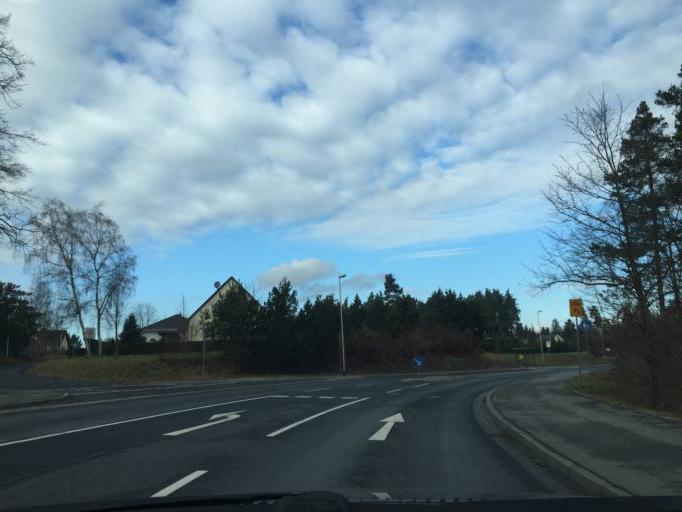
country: DE
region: Saxony
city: Ottendorf-Okrilla
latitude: 51.1852
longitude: 13.7823
